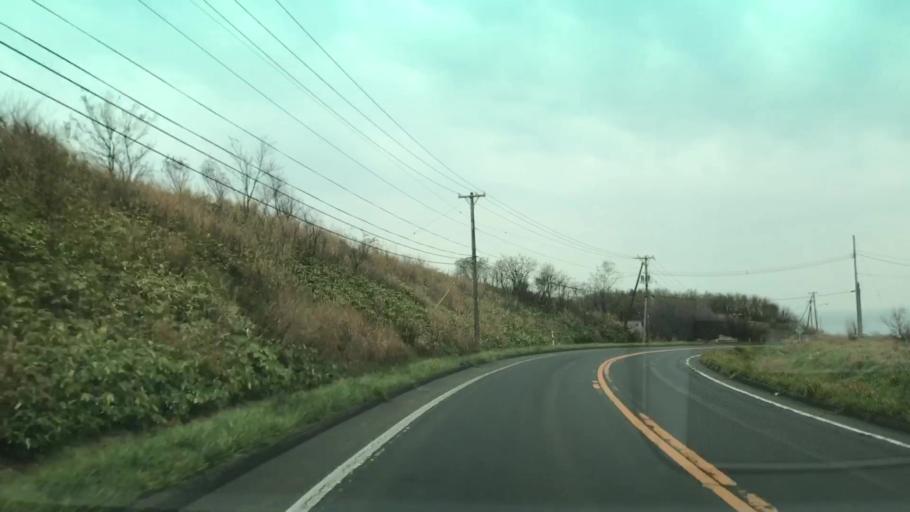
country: JP
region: Hokkaido
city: Ishikari
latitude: 43.3849
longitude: 141.4328
